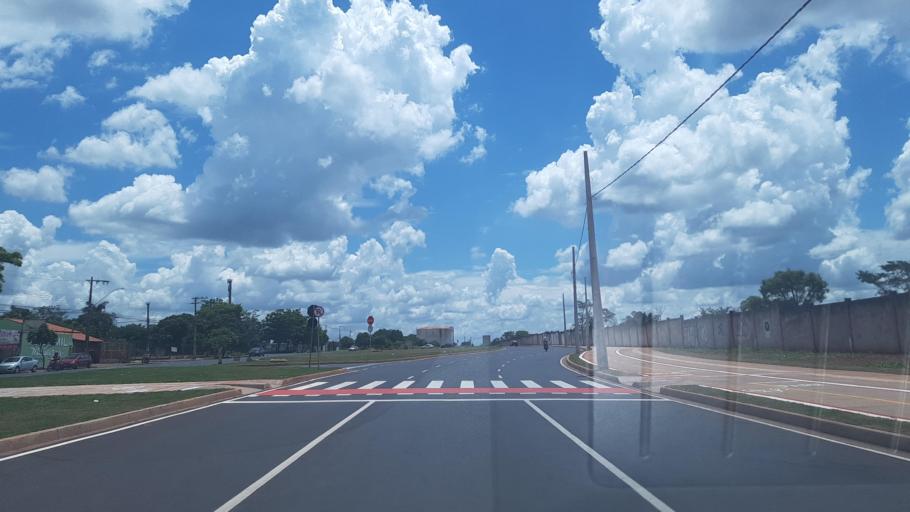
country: BR
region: Minas Gerais
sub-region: Uberlandia
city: Uberlandia
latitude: -18.9564
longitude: -48.3319
